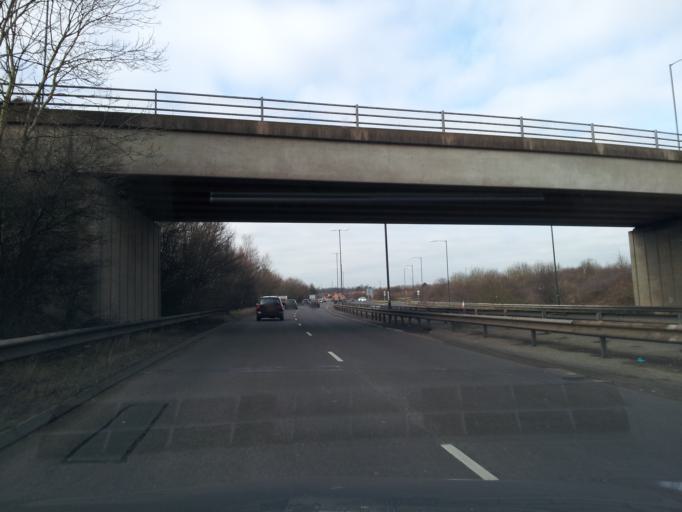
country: GB
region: England
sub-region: Derby
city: Derby
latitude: 52.9165
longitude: -1.4312
